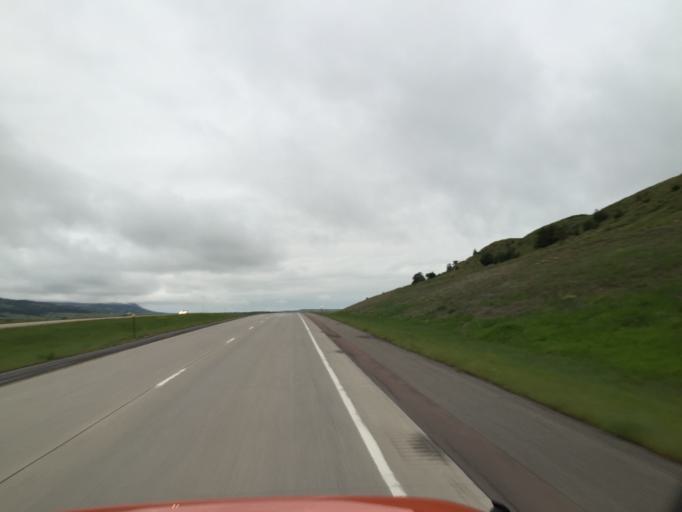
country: US
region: South Dakota
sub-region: Fall River County
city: Hot Springs
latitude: 43.4217
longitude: -103.3852
